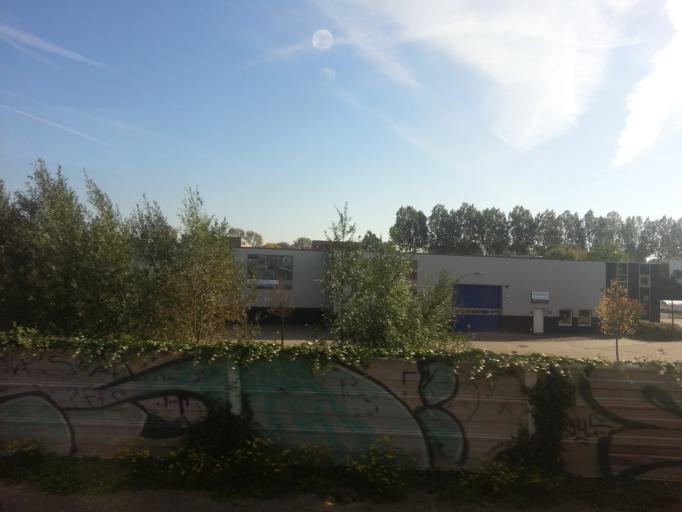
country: NL
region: Utrecht
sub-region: Stichtse Vecht
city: Breukelen
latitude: 52.1747
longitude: 4.9914
